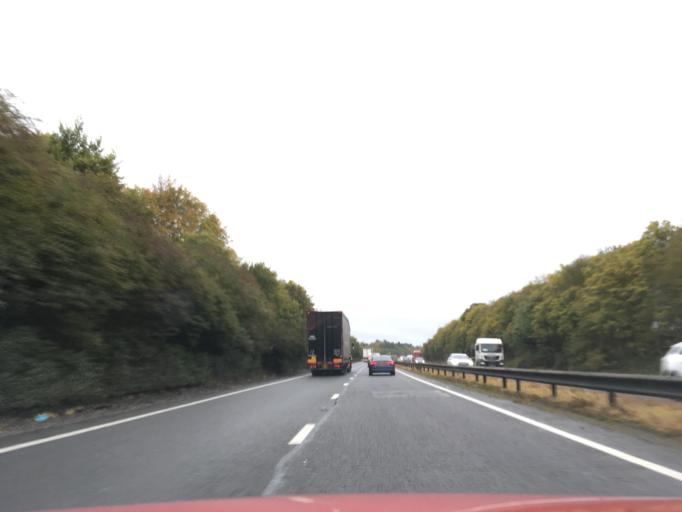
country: GB
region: England
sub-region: Hampshire
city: Kings Worthy
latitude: 51.1395
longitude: -1.3462
